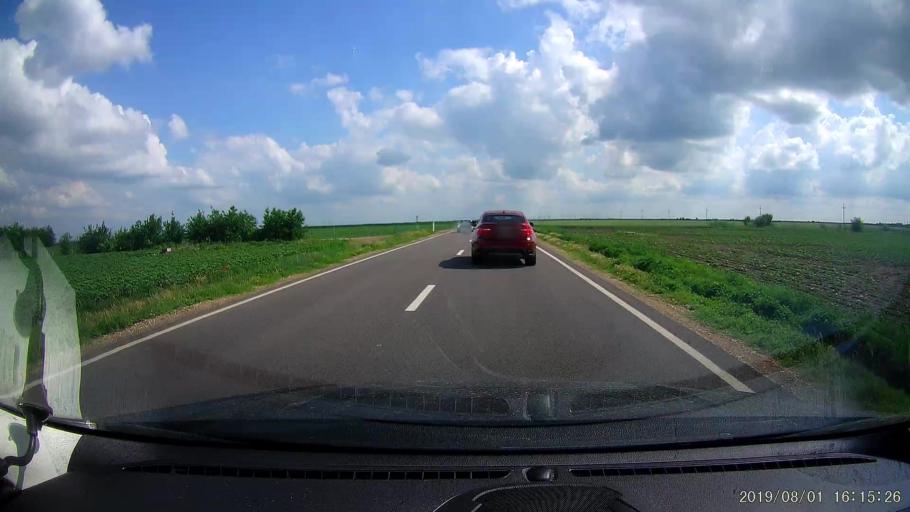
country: RO
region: Calarasi
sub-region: Comuna Stefan Voda
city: Stefan Voda
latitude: 44.3379
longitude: 27.3611
